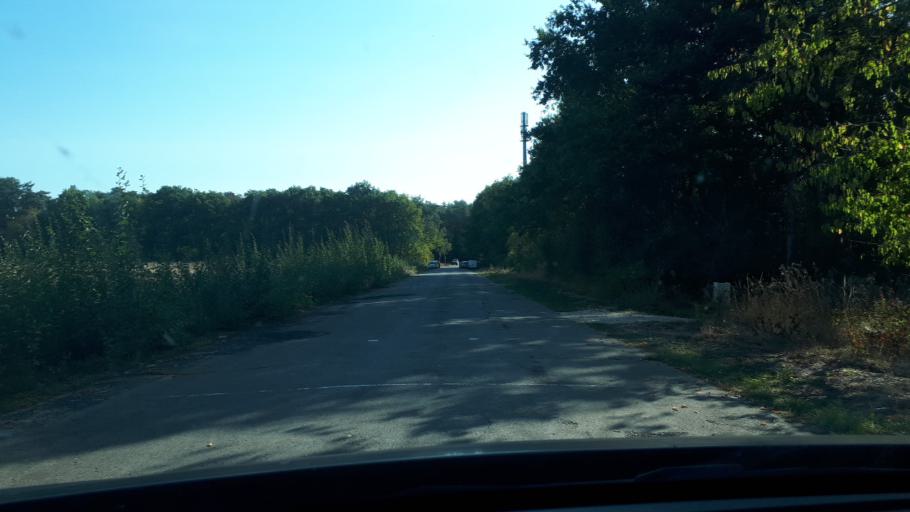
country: FR
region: Centre
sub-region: Departement du Loir-et-Cher
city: Villiers-sur-Loir
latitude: 47.8171
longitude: 1.0192
